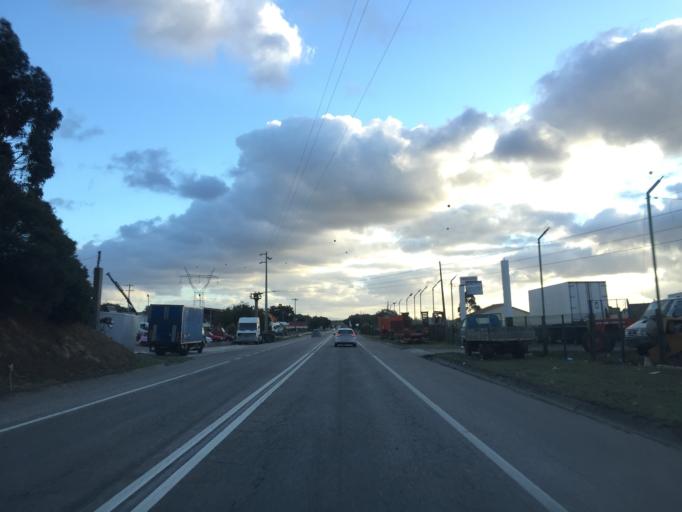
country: PT
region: Leiria
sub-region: Alcobaca
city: Benedita
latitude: 39.4399
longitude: -8.9542
